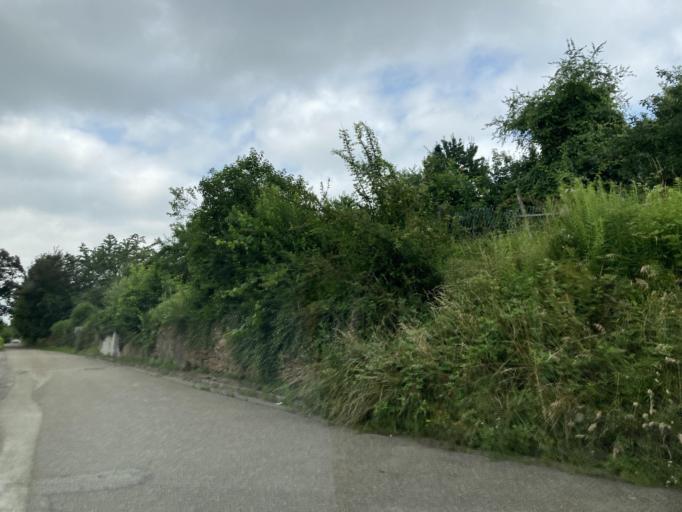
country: DE
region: Baden-Wuerttemberg
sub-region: Freiburg Region
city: Badenweiler
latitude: 47.8075
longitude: 7.6556
